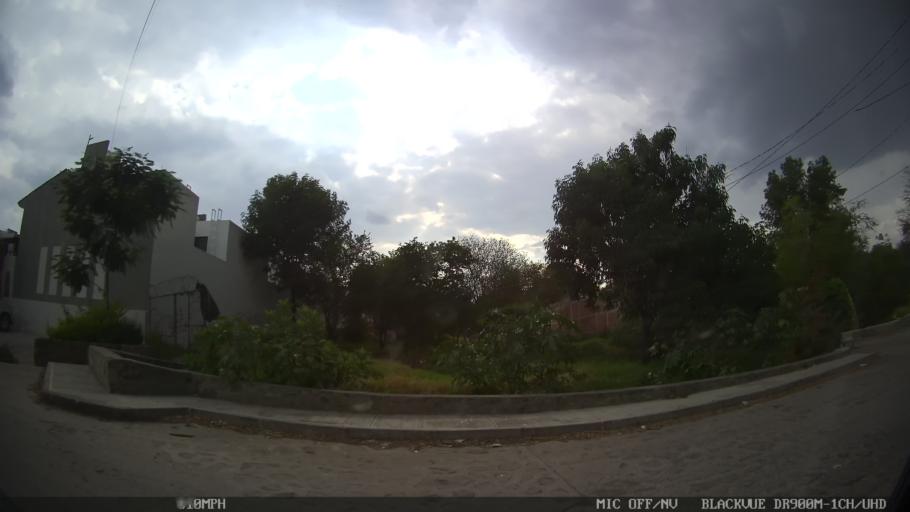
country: MX
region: Jalisco
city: Tlaquepaque
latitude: 20.6250
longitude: -103.2702
